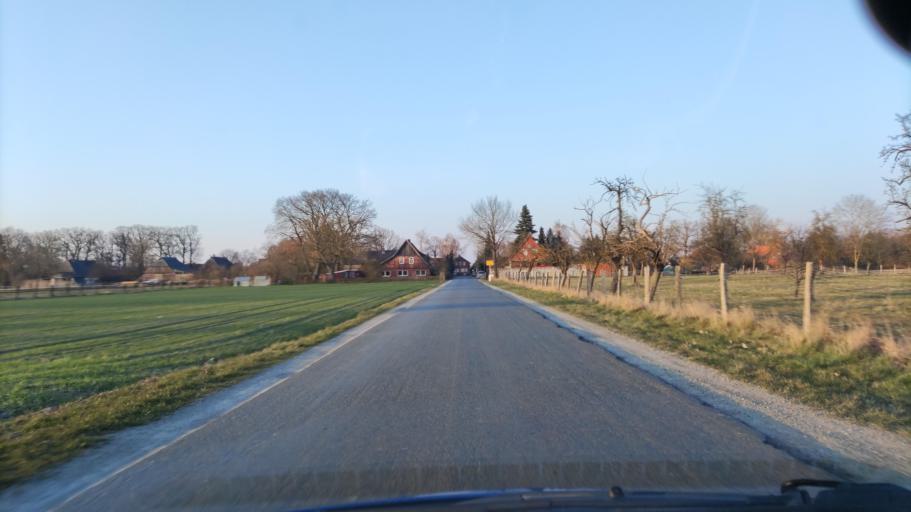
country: DE
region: Lower Saxony
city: Dannenberg
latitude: 53.1071
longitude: 11.1347
